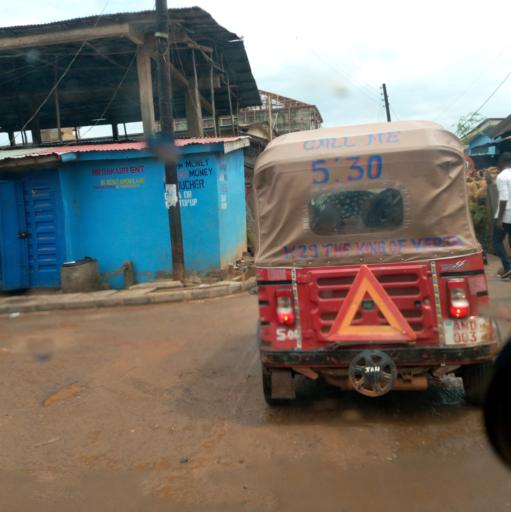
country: SL
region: Western Area
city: Freetown
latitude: 8.4751
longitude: -13.2370
